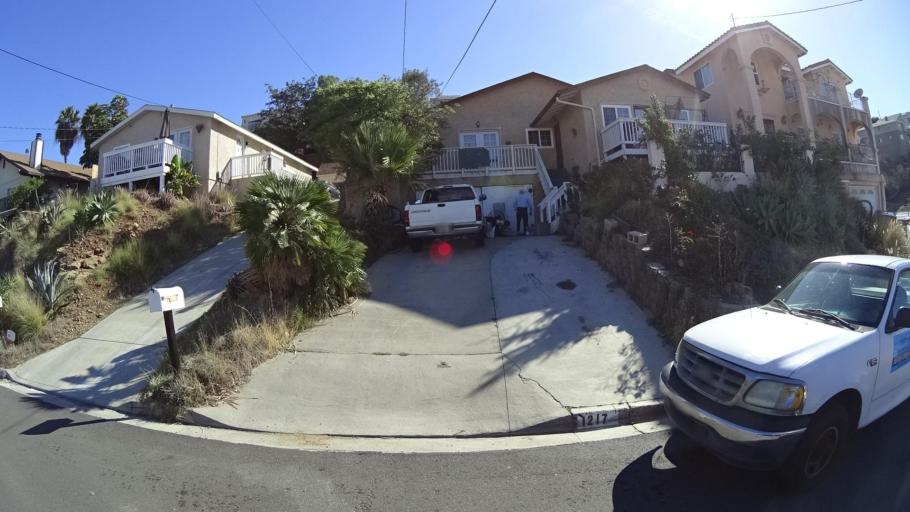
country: US
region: California
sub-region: San Diego County
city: La Presa
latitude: 32.7171
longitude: -116.9883
